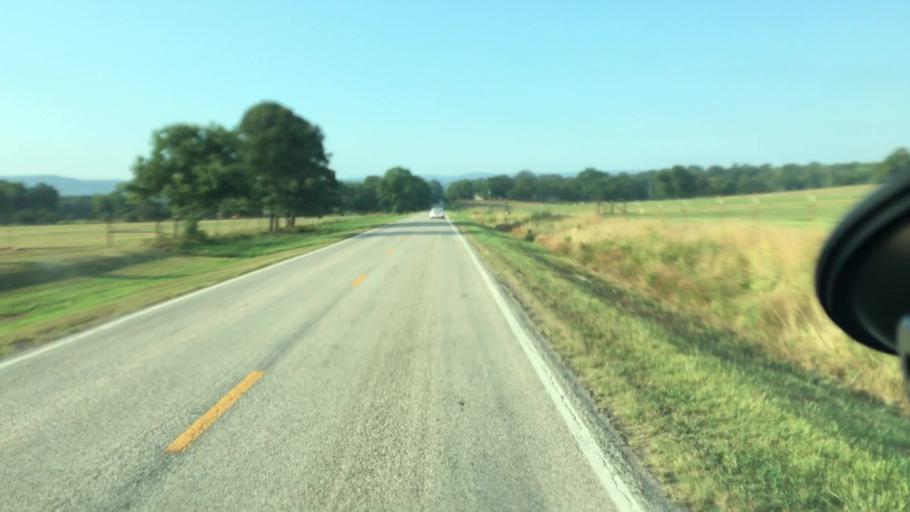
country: US
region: Arkansas
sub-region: Logan County
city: Paris
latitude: 35.3225
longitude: -93.6322
